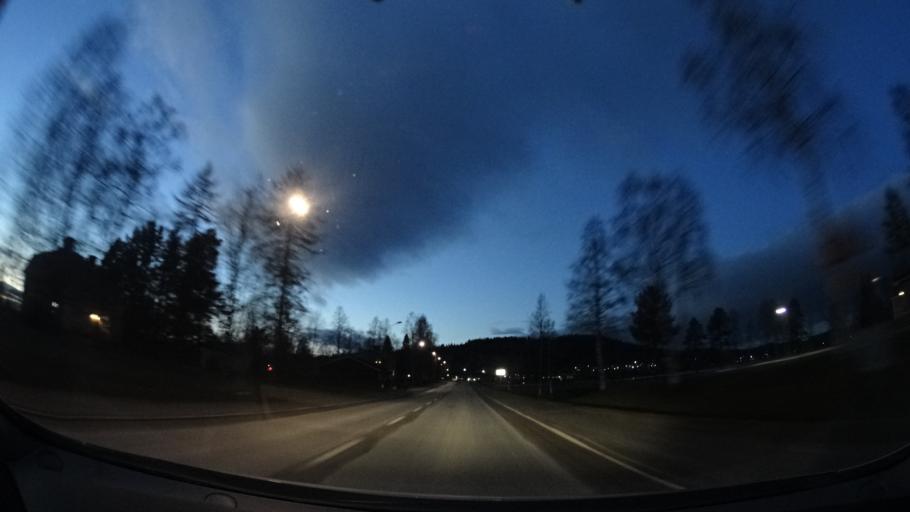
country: SE
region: Vaesterbotten
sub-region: Dorotea Kommun
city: Dorotea
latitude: 64.2608
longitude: 16.4218
